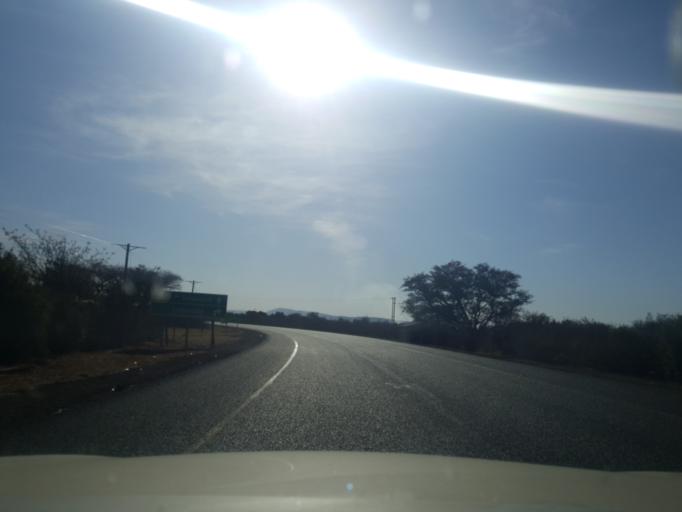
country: ZA
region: North-West
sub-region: Ngaka Modiri Molema District Municipality
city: Zeerust
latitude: -25.5064
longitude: 25.9891
